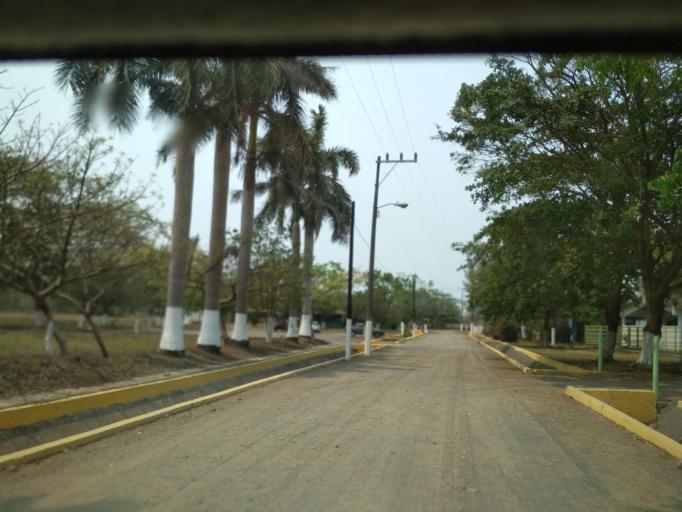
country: MX
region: Veracruz
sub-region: Veracruz
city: Lomas de Rio Medio Cuatro
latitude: 19.1713
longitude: -96.2117
